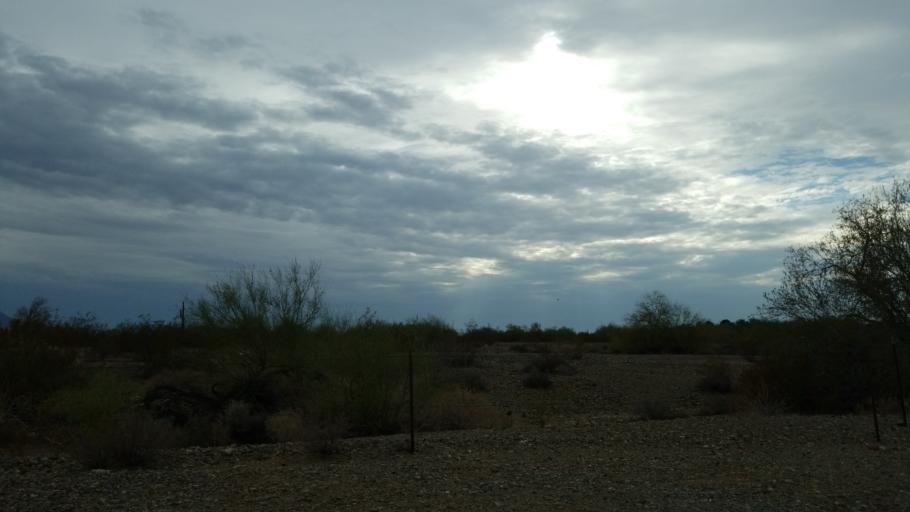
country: US
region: Arizona
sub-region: Maricopa County
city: Laveen
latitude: 33.3585
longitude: -112.0920
